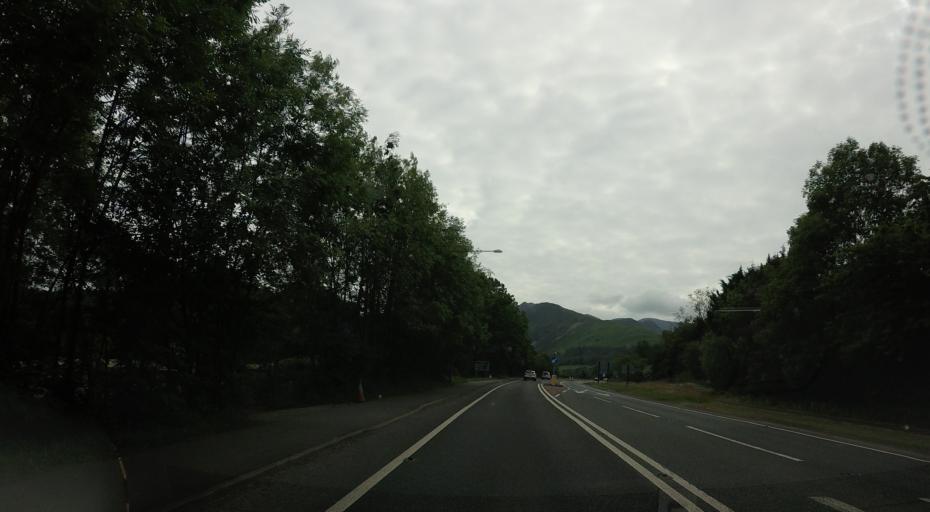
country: GB
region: England
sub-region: Cumbria
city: Keswick
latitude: 54.6024
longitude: -3.1681
